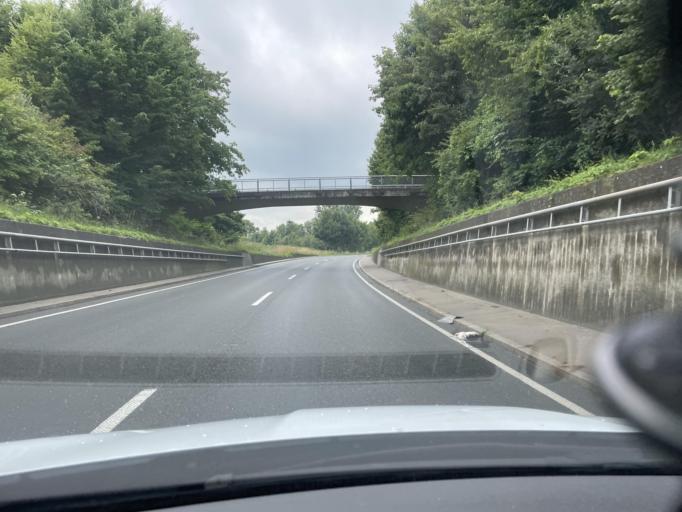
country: DE
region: Bavaria
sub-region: Upper Bavaria
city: Schechen
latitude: 47.9514
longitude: 12.1290
